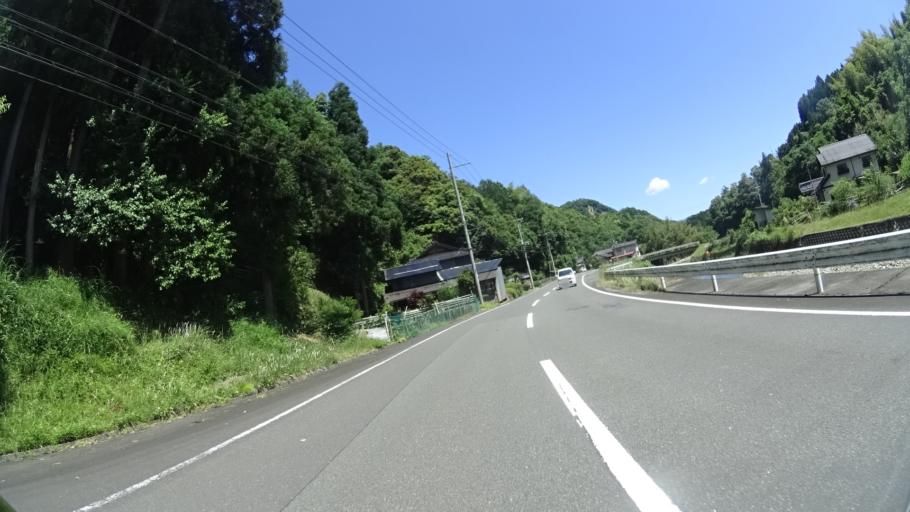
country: JP
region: Kyoto
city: Miyazu
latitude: 35.4385
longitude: 135.2027
